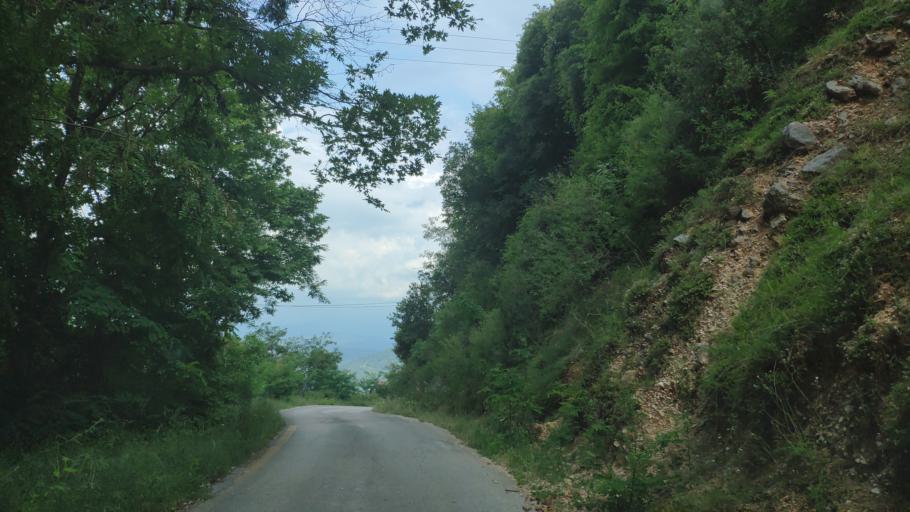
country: GR
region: Epirus
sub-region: Nomos Artas
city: Agios Dimitrios
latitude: 39.3758
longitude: 21.0248
